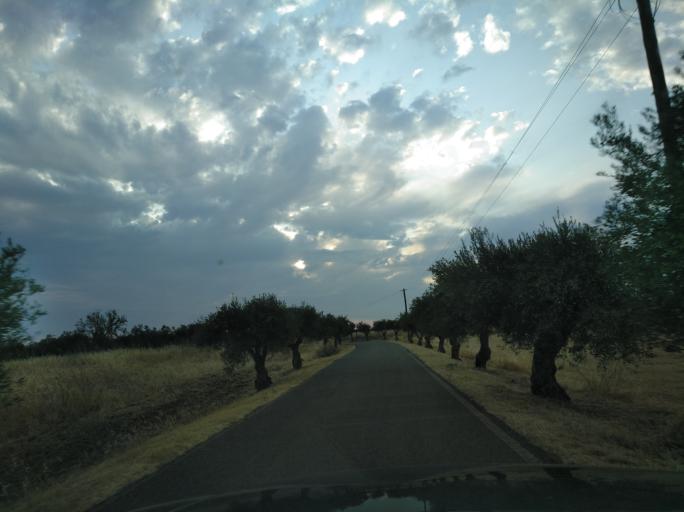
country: PT
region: Portalegre
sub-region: Campo Maior
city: Campo Maior
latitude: 39.0162
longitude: -7.0355
